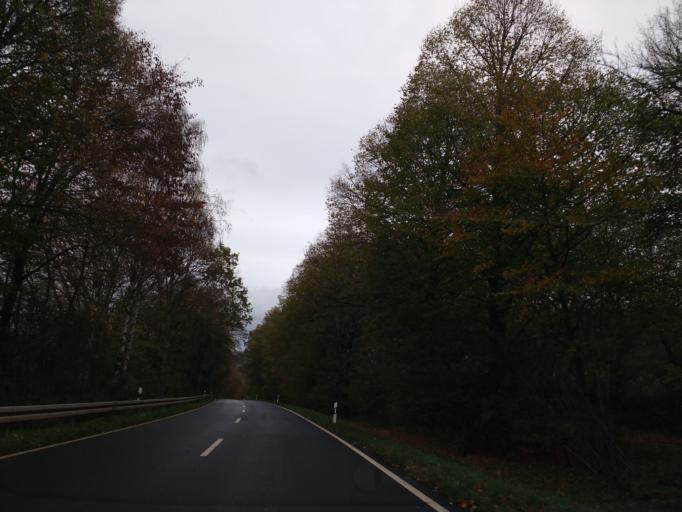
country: DE
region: Hesse
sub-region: Regierungsbezirk Kassel
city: Sachsenhausen
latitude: 51.2094
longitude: 8.9909
